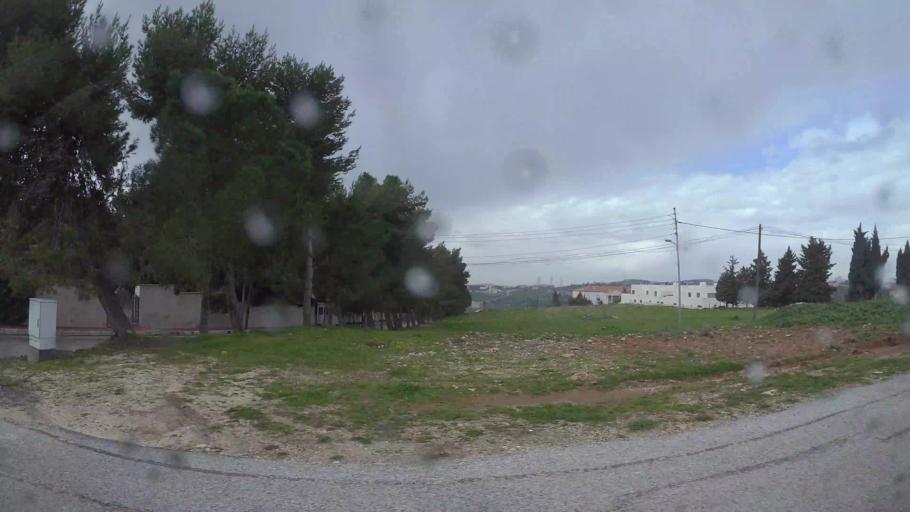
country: JO
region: Amman
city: Wadi as Sir
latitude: 31.9854
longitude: 35.8196
